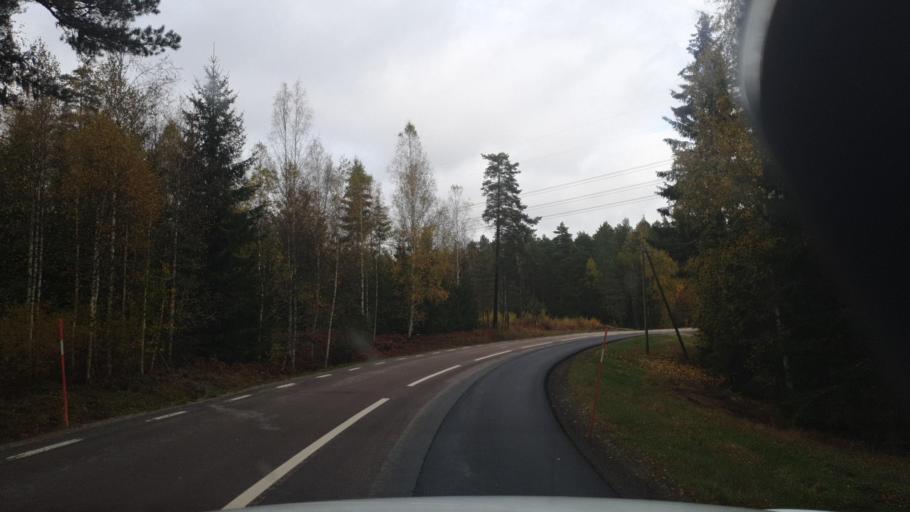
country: SE
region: Vaermland
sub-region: Sunne Kommun
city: Sunne
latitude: 59.6673
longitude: 12.9680
